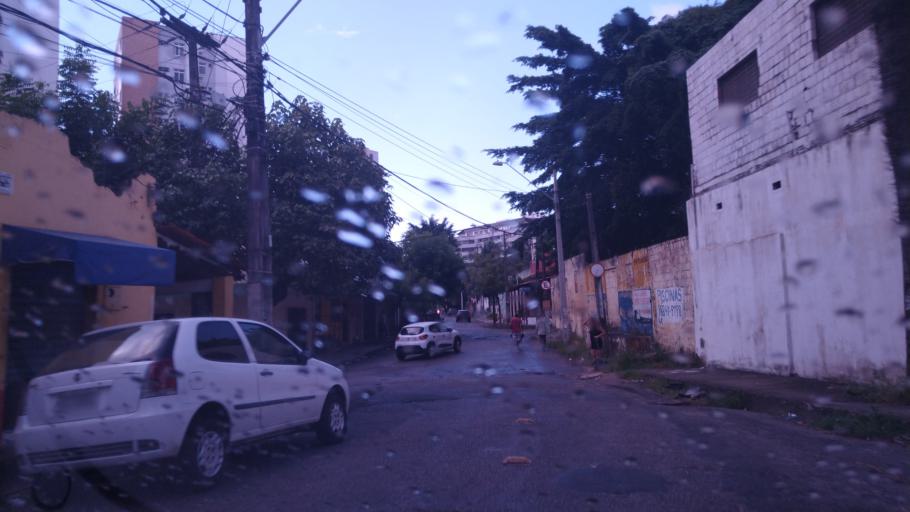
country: BR
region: Ceara
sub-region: Fortaleza
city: Fortaleza
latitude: -3.7290
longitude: -38.4884
